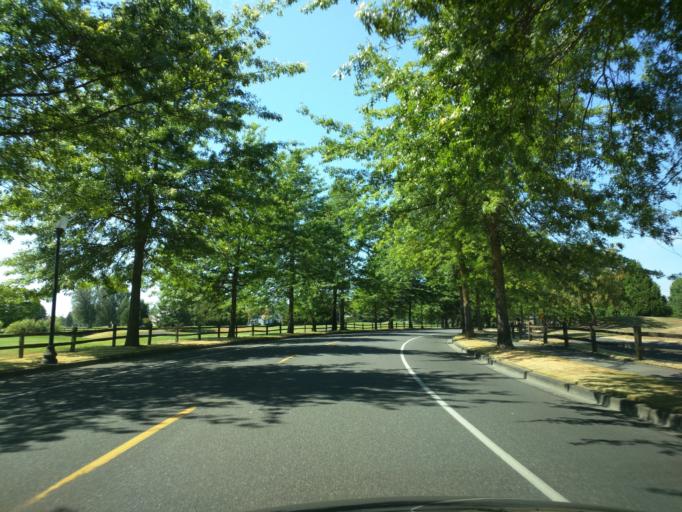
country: US
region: Washington
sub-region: Whatcom County
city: Lynden
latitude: 48.9582
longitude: -122.4439
